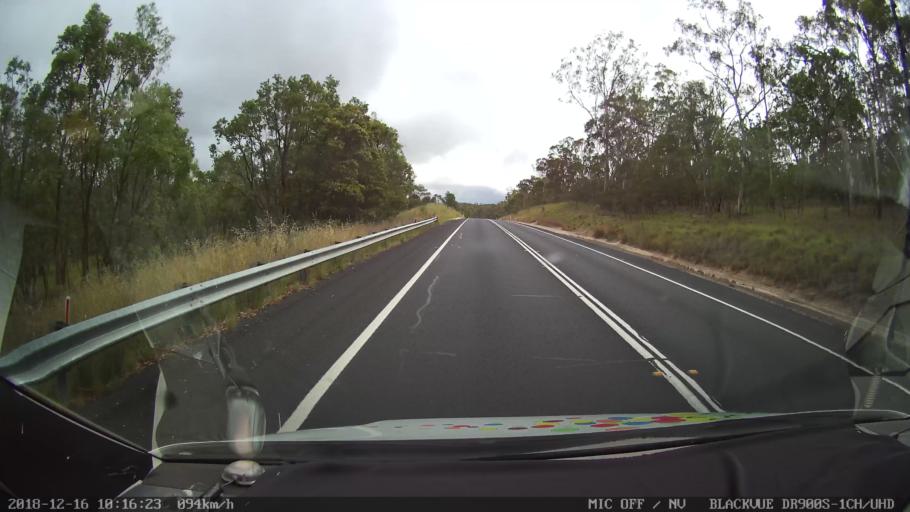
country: AU
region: New South Wales
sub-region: Tenterfield Municipality
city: Carrolls Creek
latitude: -29.2672
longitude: 151.9823
